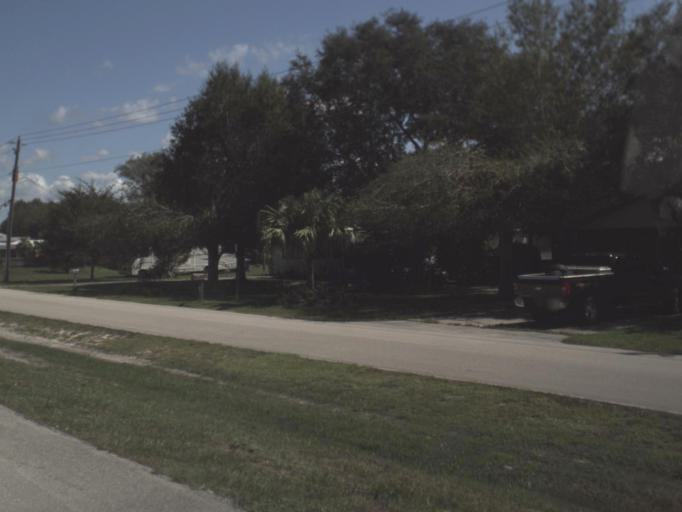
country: US
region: Florida
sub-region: Glades County
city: Buckhead Ridge
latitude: 27.1370
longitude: -80.8913
